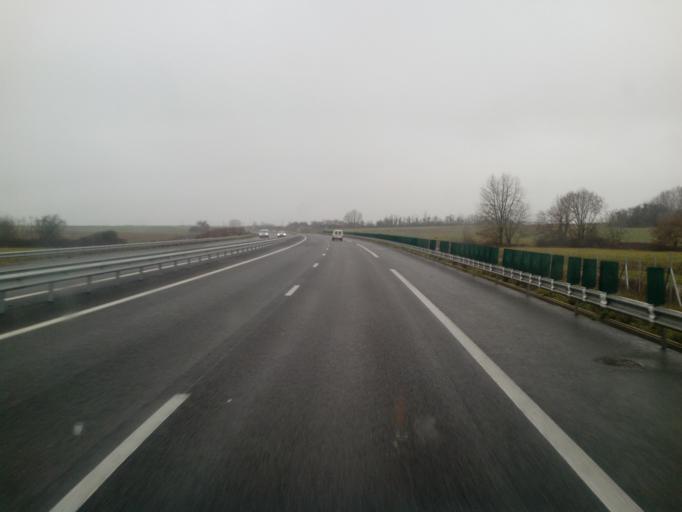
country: FR
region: Poitou-Charentes
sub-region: Departement de la Vienne
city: Terce
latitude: 46.4850
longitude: 0.5289
